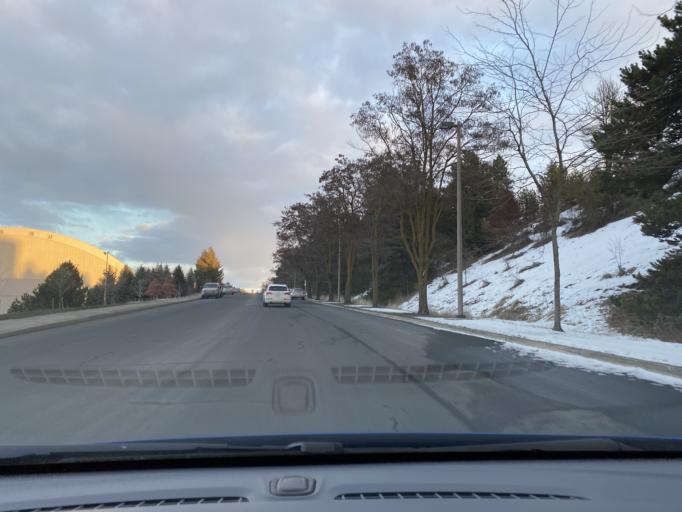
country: US
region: Idaho
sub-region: Latah County
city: Moscow
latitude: 46.7257
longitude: -117.0221
